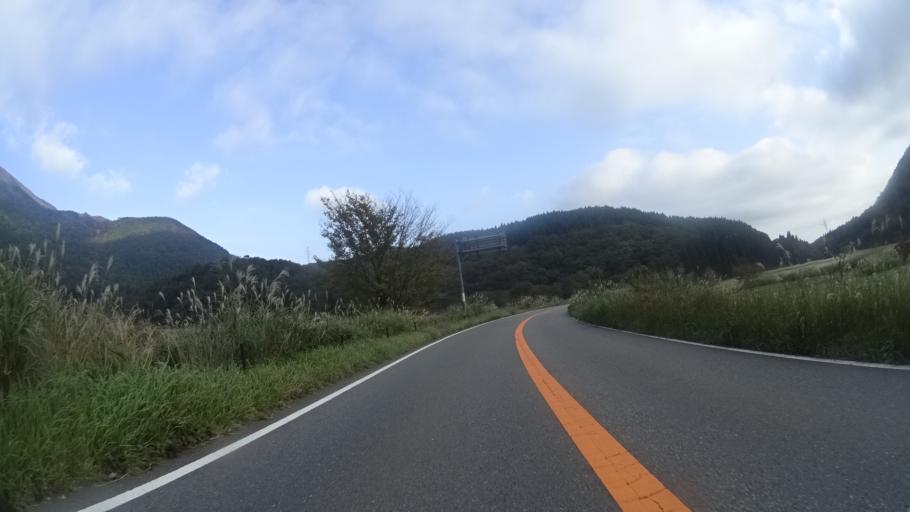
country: JP
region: Oita
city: Beppu
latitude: 33.2749
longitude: 131.4146
